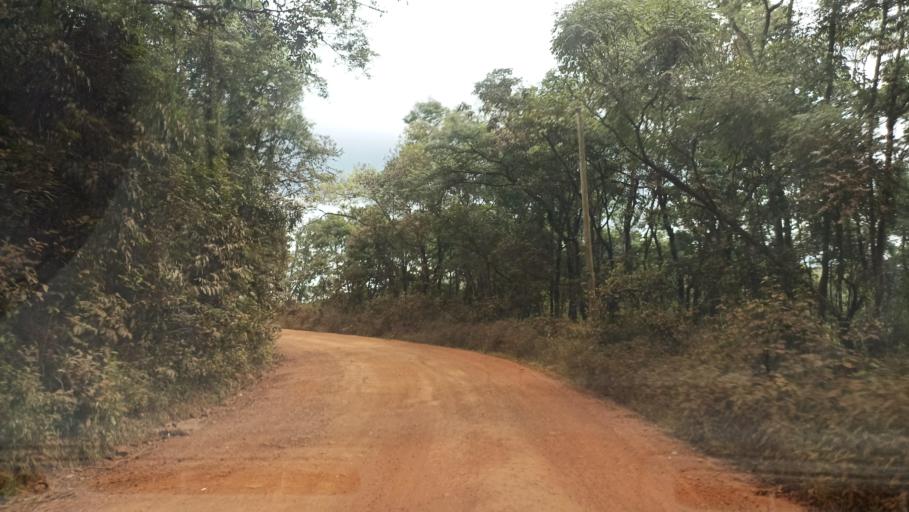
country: BR
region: Minas Gerais
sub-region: Itabirito
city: Itabirito
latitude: -20.3815
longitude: -43.7604
